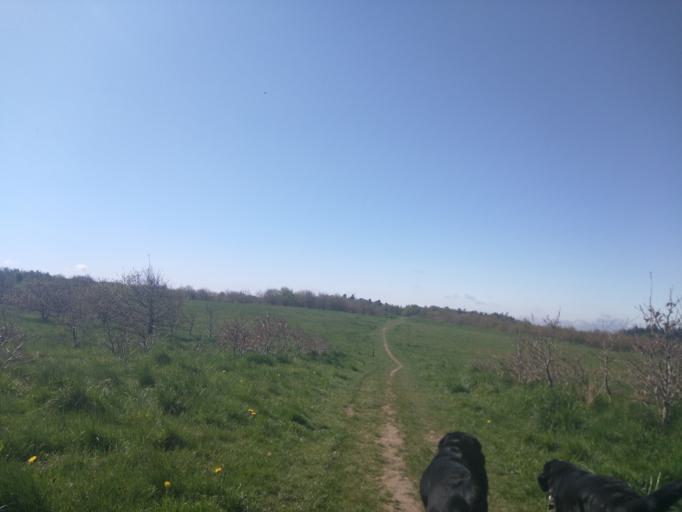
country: DK
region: Central Jutland
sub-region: Viborg Kommune
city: Viborg
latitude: 56.4444
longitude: 9.4329
